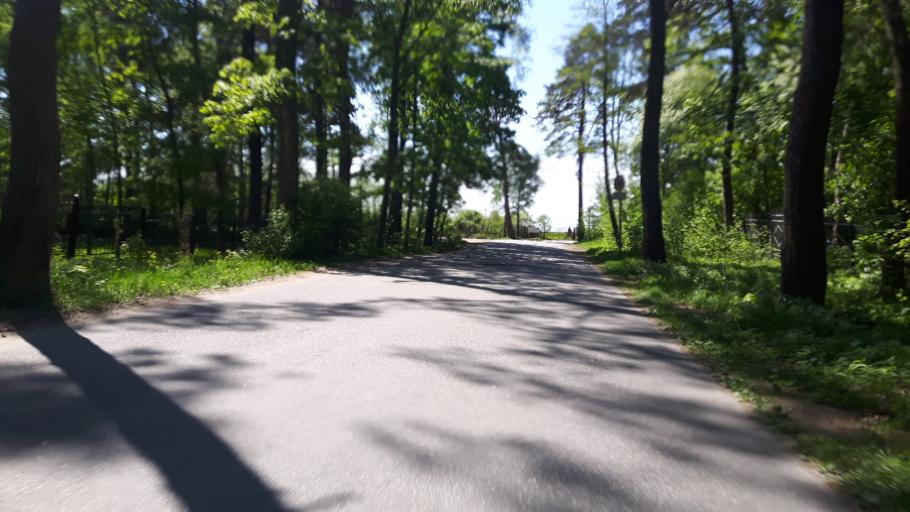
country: RU
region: St.-Petersburg
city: Zelenogorsk
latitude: 60.1887
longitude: 29.7064
